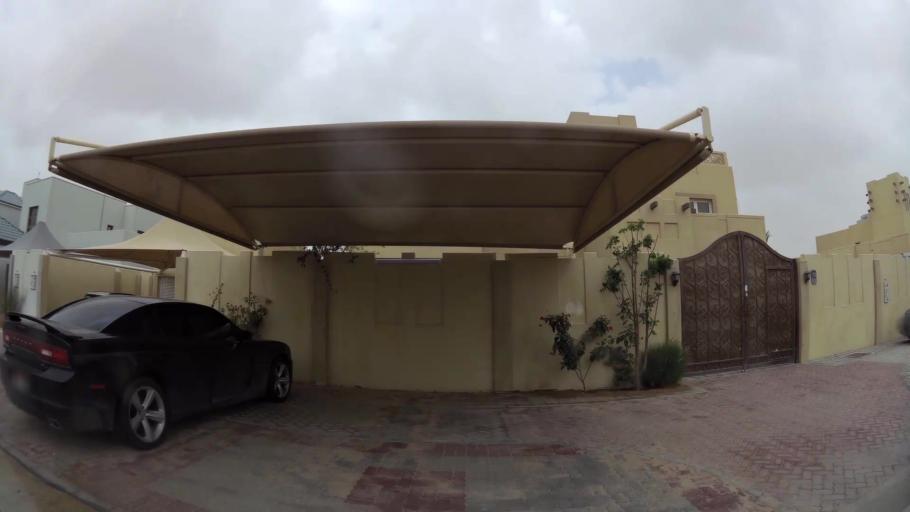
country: AE
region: Abu Dhabi
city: Abu Dhabi
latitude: 24.4515
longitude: 54.7115
